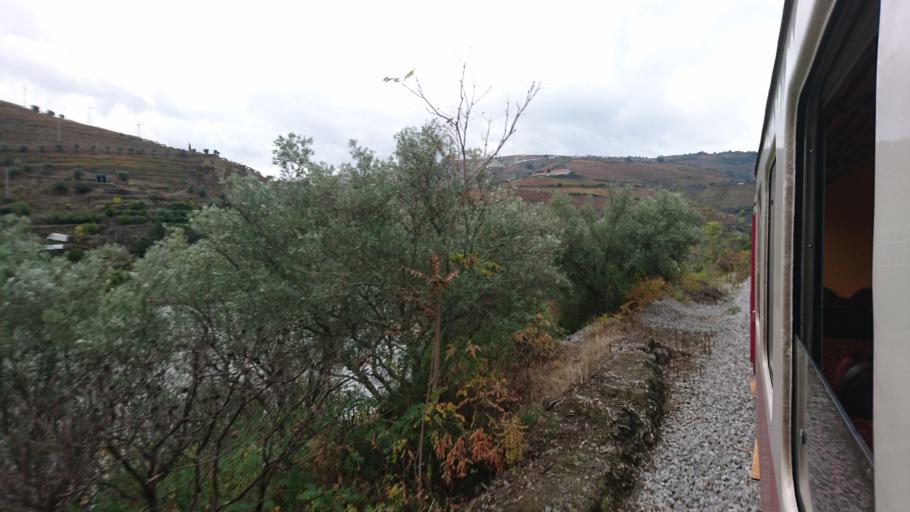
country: PT
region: Viseu
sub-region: Tabuaco
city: Tabuaco
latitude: 41.1796
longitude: -7.5535
